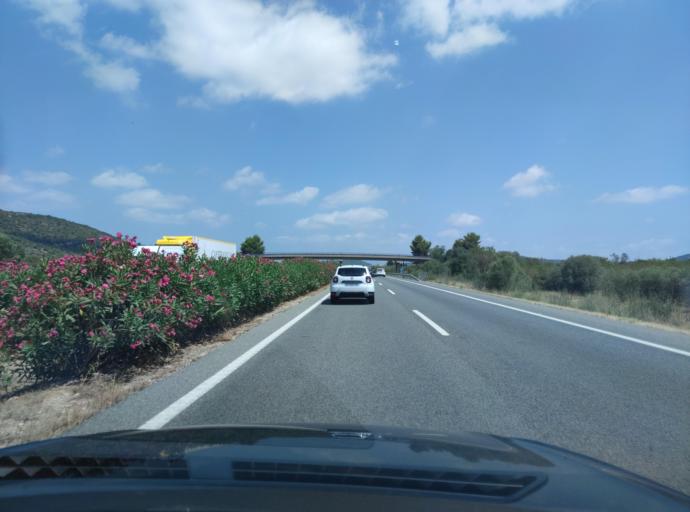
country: ES
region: Catalonia
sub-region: Provincia de Tarragona
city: Ulldecona
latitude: 40.6421
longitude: 0.5031
